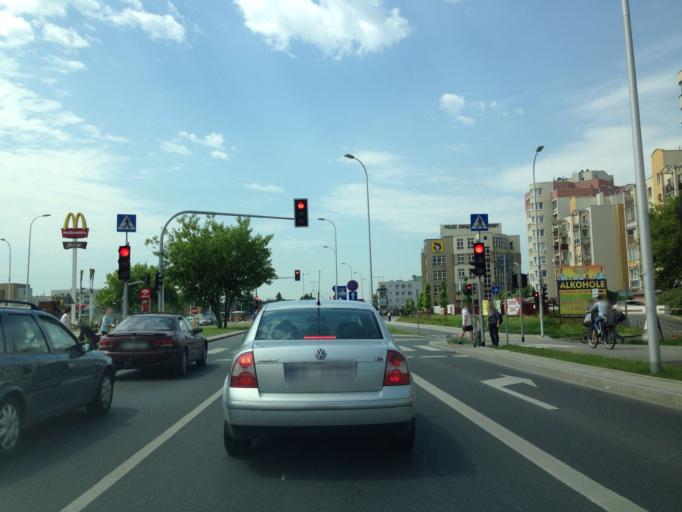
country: PL
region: Masovian Voivodeship
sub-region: Warszawa
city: Bemowo
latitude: 52.2396
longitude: 20.8998
